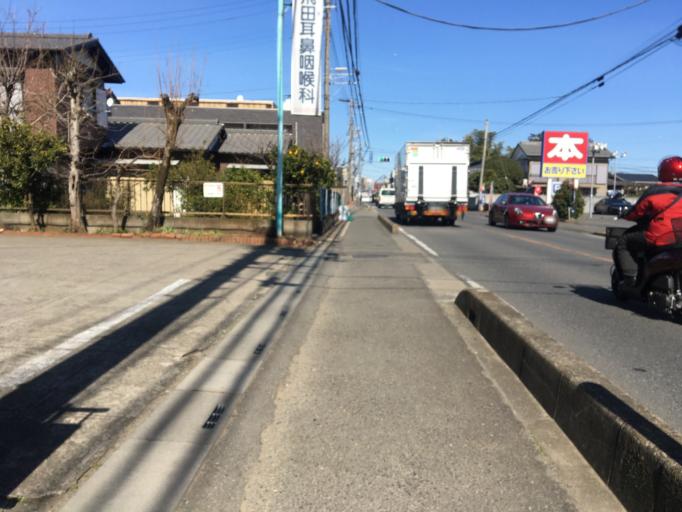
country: JP
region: Saitama
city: Shiki
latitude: 35.8120
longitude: 139.5665
